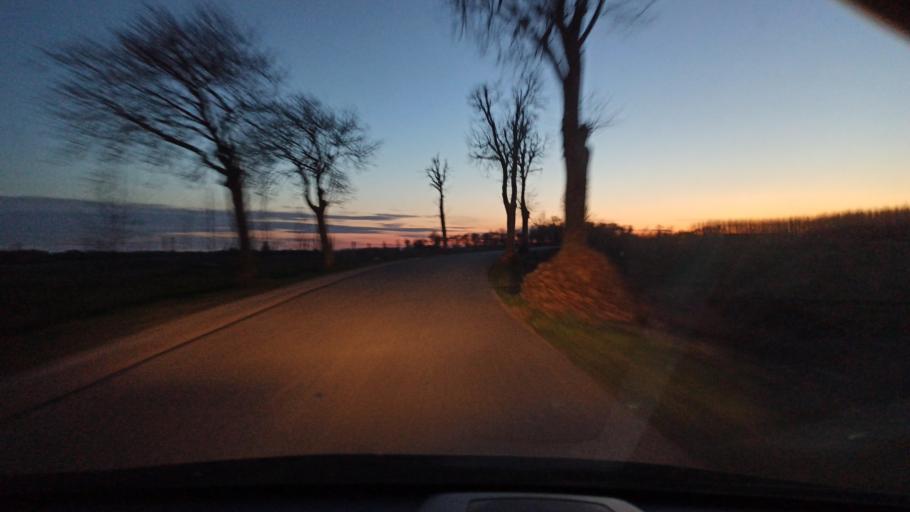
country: PL
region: Warmian-Masurian Voivodeship
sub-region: Powiat elblaski
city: Gronowo Gorne
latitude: 54.1802
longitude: 19.5320
